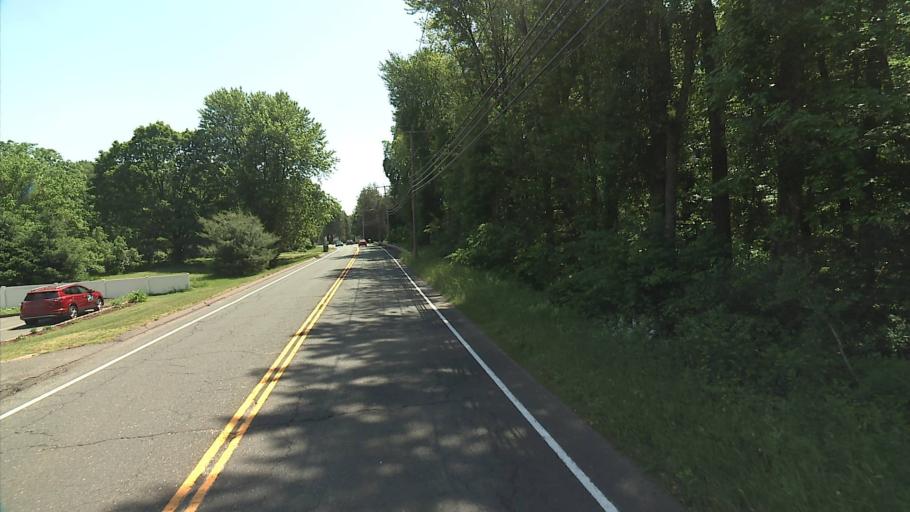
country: US
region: Connecticut
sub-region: Hartford County
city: South Windsor
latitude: 41.8261
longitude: -72.5700
